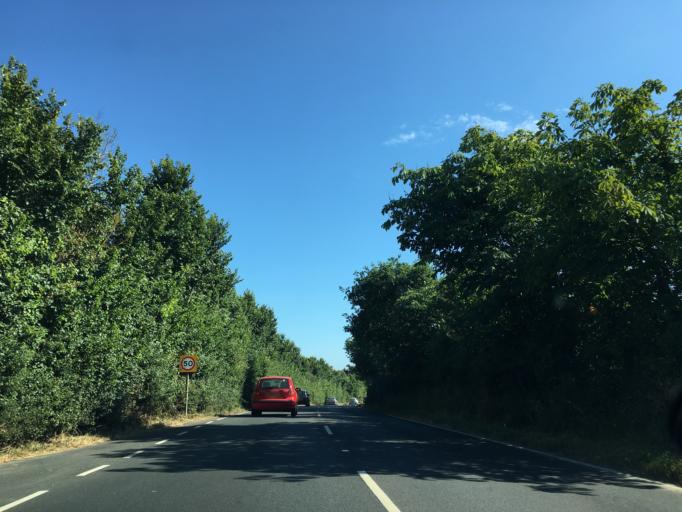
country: GB
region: England
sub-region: Isle of Wight
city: Brading
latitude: 50.6897
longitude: -1.1439
